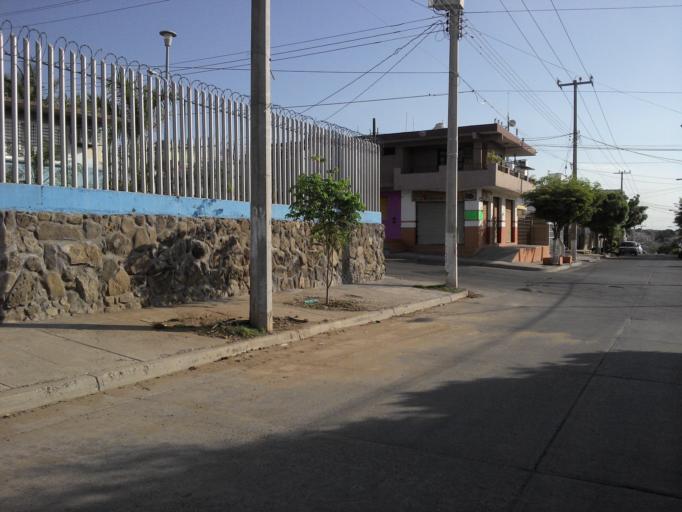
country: MX
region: Sinaloa
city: Culiacan
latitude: 24.7928
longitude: -107.4068
